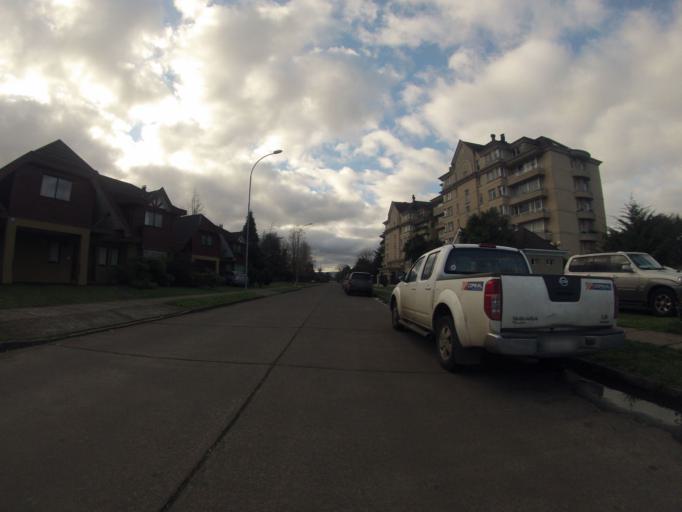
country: CL
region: Araucania
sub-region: Provincia de Cautin
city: Temuco
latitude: -38.7406
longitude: -72.6394
